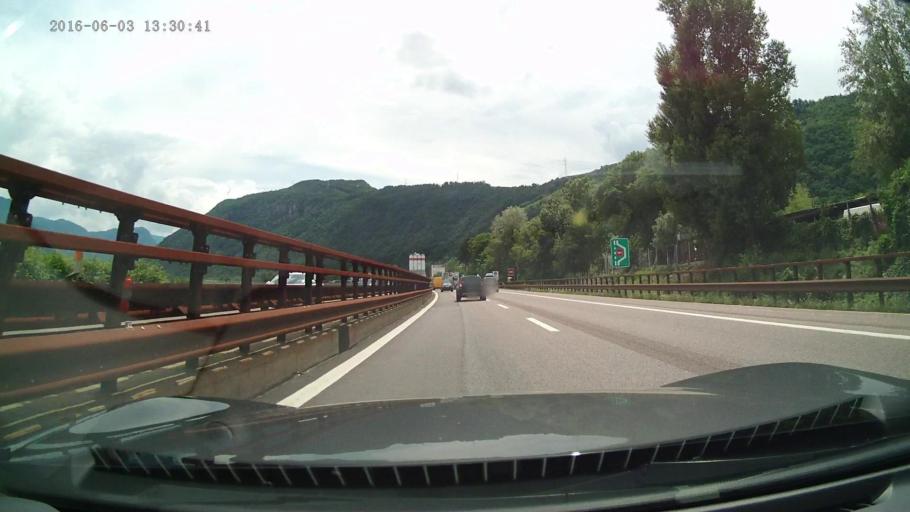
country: IT
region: Trentino-Alto Adige
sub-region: Bolzano
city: Cornaiano
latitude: 46.4626
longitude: 11.3045
